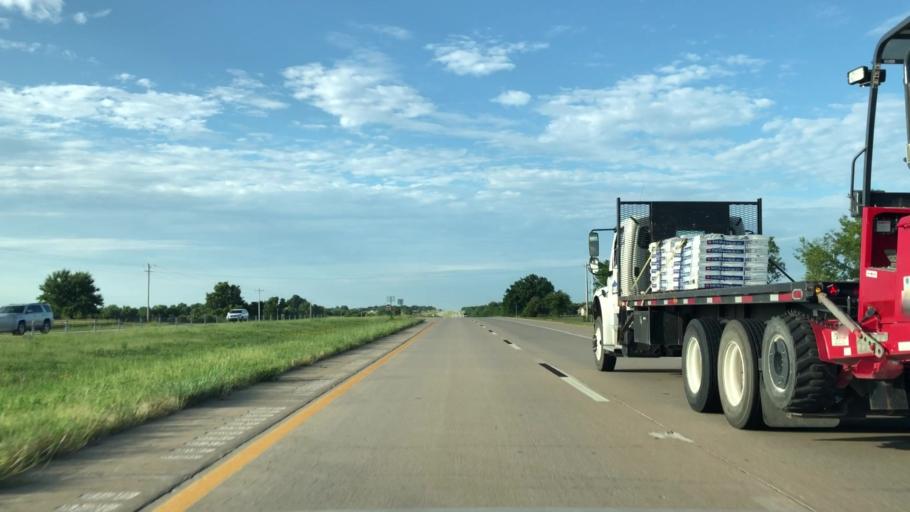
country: US
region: Oklahoma
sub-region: Osage County
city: Skiatook
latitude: 36.4468
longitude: -95.9207
